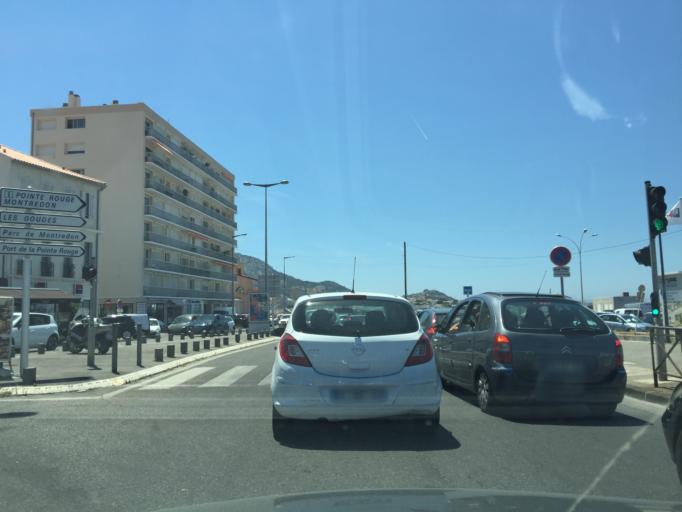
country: FR
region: Provence-Alpes-Cote d'Azur
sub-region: Departement des Bouches-du-Rhone
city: Marseille 08
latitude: 43.2481
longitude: 5.3747
